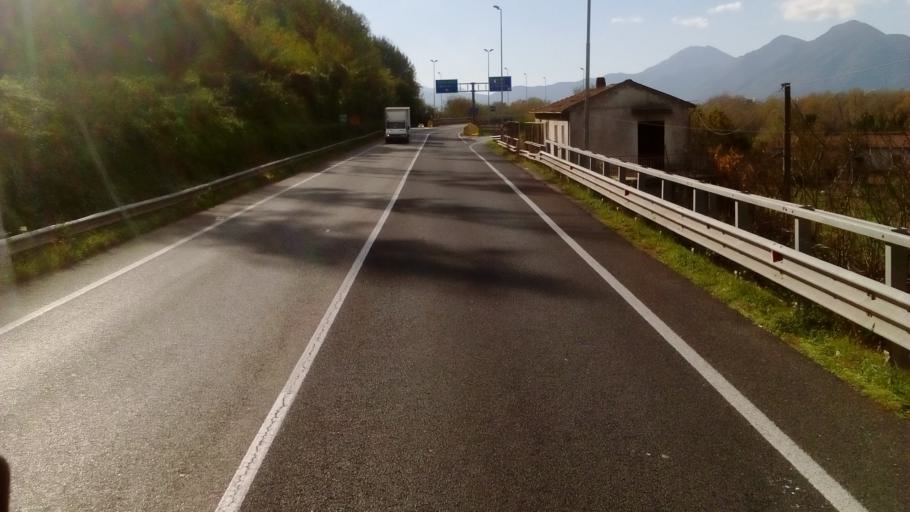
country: IT
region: Molise
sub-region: Provincia di Isernia
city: Taverna Ravindola
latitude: 41.5201
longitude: 14.1434
